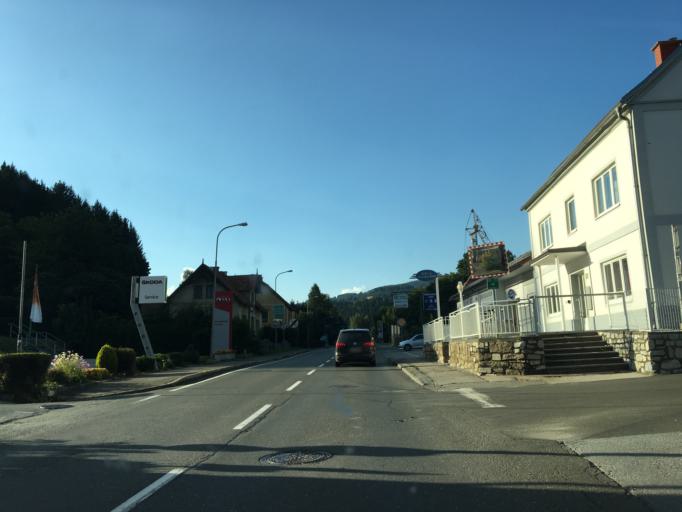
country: AT
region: Styria
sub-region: Politischer Bezirk Murau
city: Neumarkt in Steiermark
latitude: 47.0746
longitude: 14.4256
